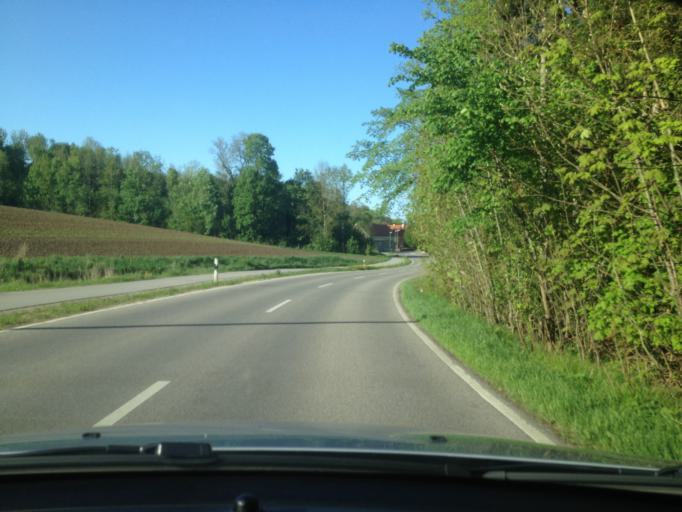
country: DE
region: Bavaria
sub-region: Swabia
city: Stadtbergen
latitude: 48.3315
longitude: 10.8234
